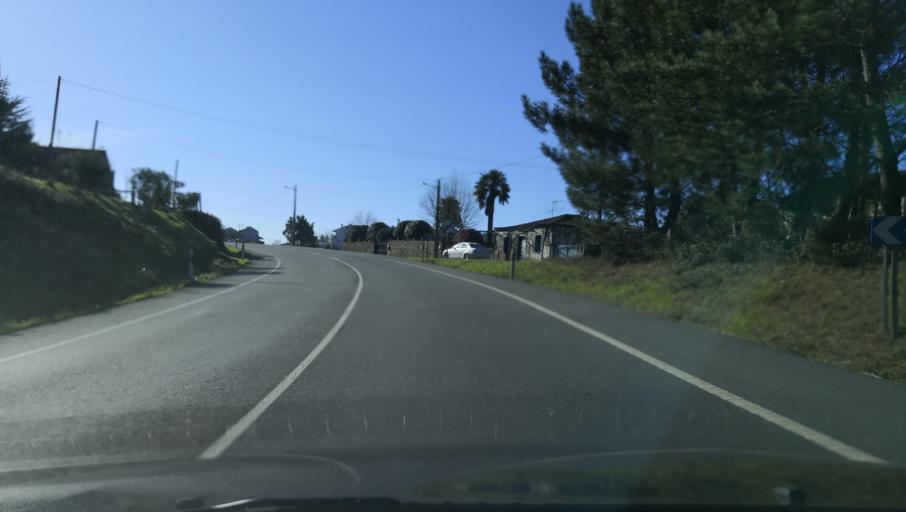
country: ES
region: Galicia
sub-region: Provincia da Coruna
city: Ribeira
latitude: 42.7644
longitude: -8.3999
